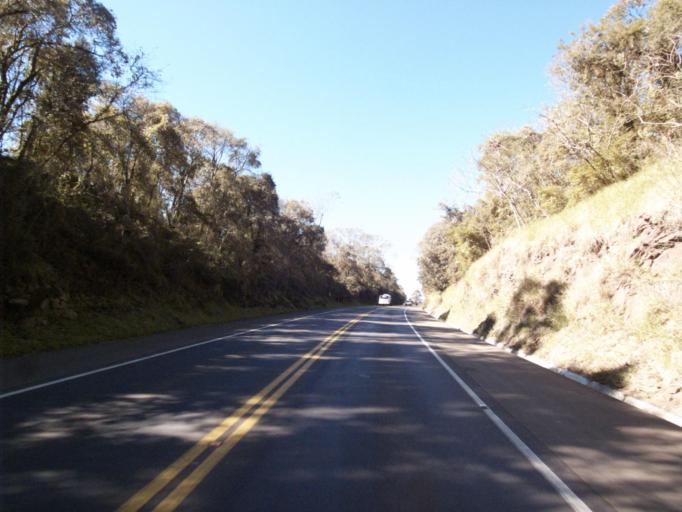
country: BR
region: Santa Catarina
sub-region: Chapeco
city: Chapeco
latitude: -26.9814
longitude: -52.5949
